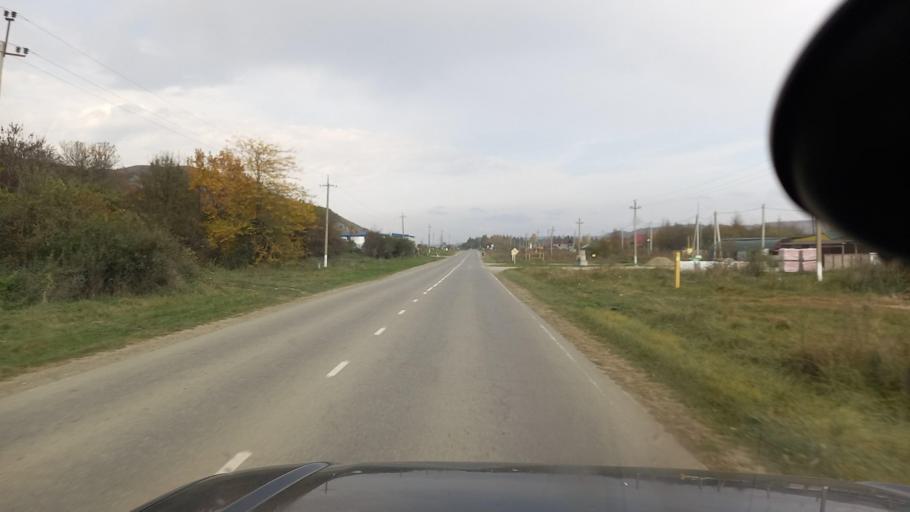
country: RU
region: Krasnodarskiy
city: Psebay
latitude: 44.1410
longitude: 40.8219
